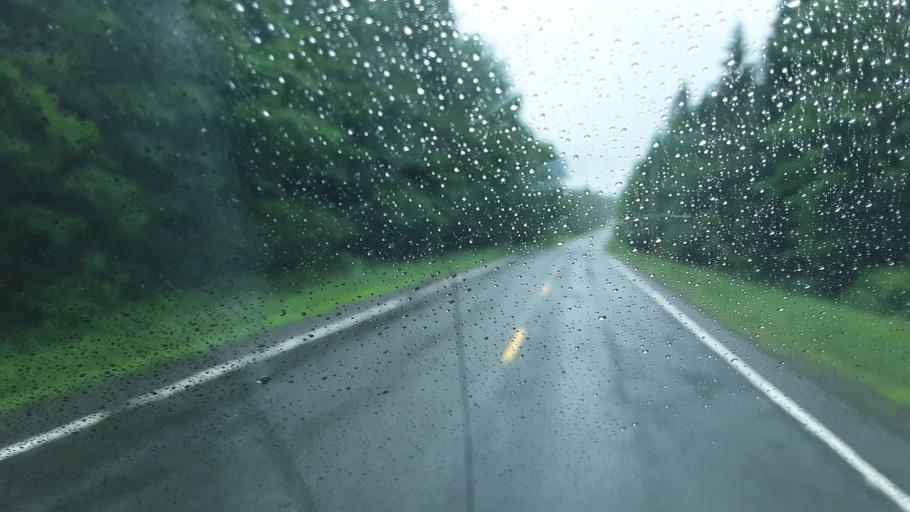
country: US
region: Maine
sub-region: Penobscot County
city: Patten
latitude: 46.1933
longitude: -68.3336
